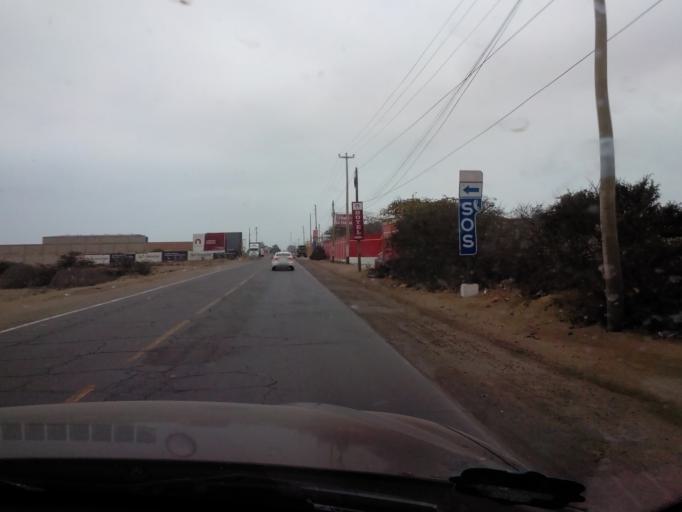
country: PE
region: Ica
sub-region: Provincia de Chincha
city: San Pedro
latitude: -13.4101
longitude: -76.1713
